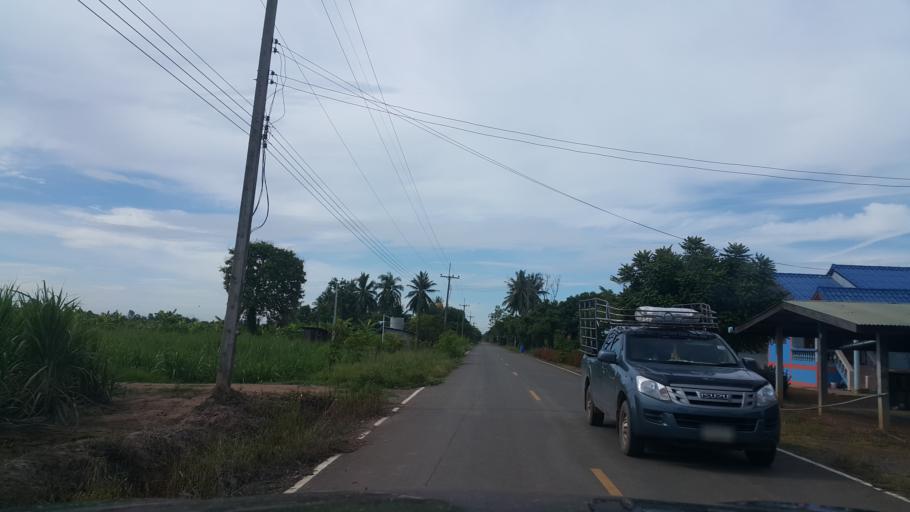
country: TH
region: Sukhothai
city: Si Nakhon
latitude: 17.2658
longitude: 99.9275
